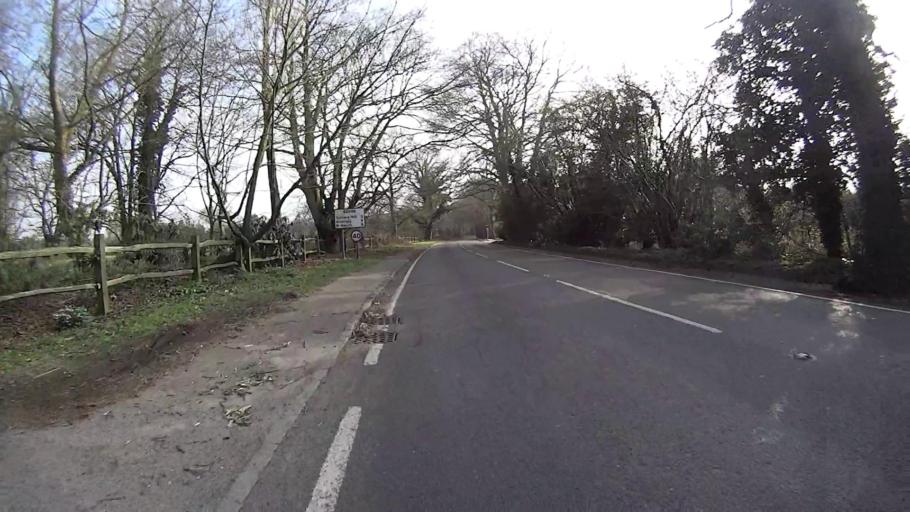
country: GB
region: England
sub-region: West Sussex
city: Crawley Down
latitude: 51.1343
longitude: -0.0923
